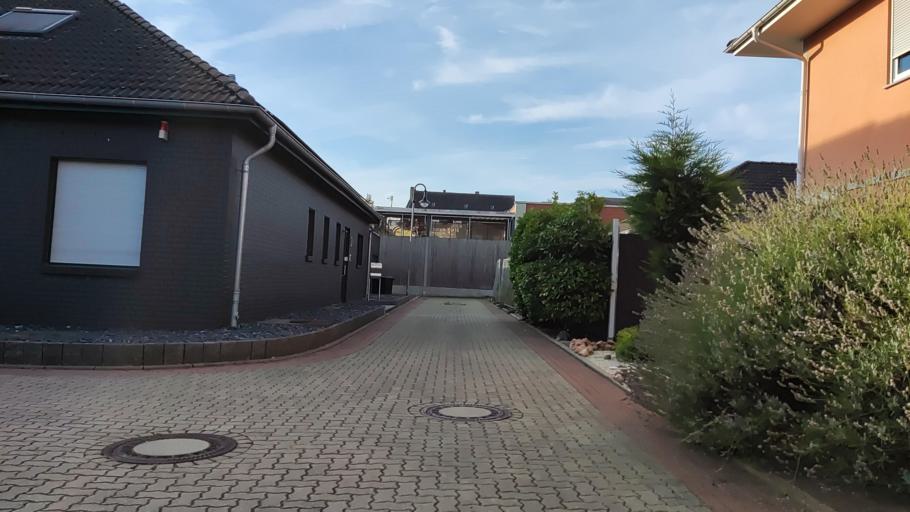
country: DE
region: North Rhine-Westphalia
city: Castrop-Rauxel
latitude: 51.5497
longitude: 7.2795
